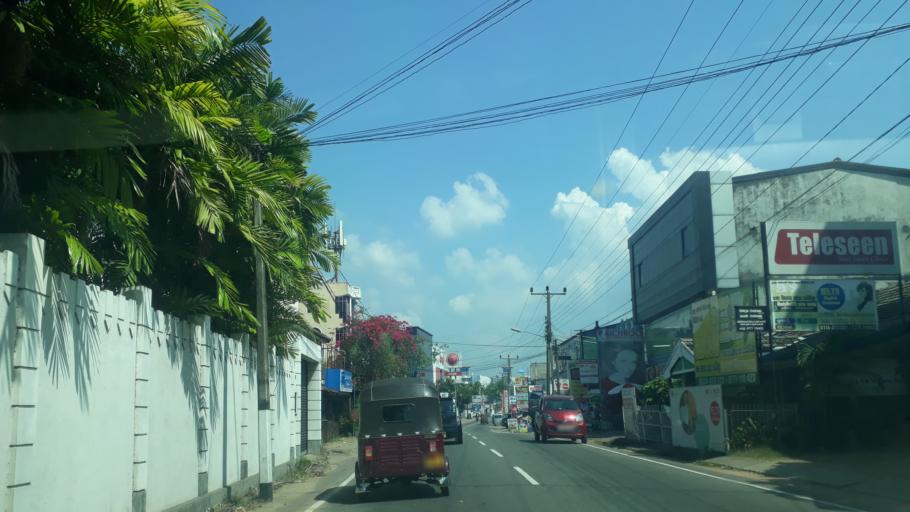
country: LK
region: Western
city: Gampaha
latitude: 7.0901
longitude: 80.0029
